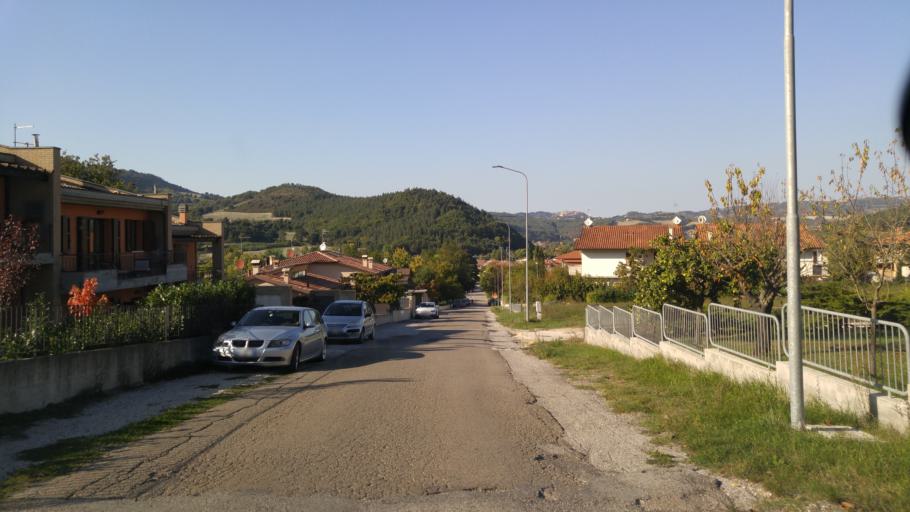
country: IT
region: The Marches
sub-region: Provincia di Pesaro e Urbino
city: Fermignano
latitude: 43.6660
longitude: 12.6452
